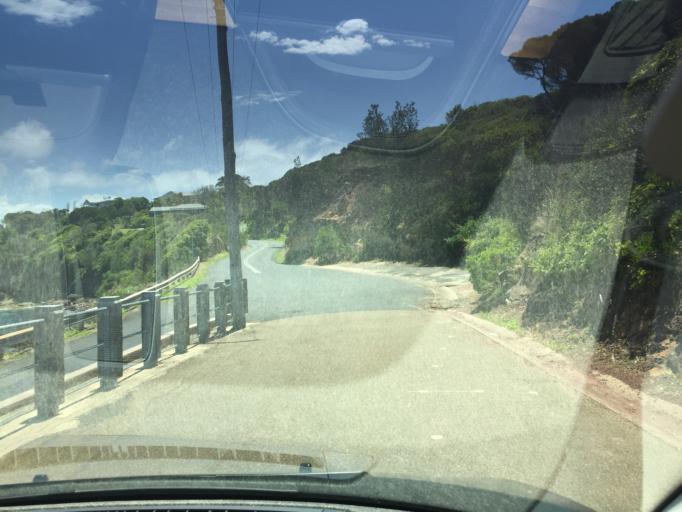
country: AU
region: New South Wales
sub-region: Bega Valley
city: Merimbula
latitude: -36.8984
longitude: 149.9274
